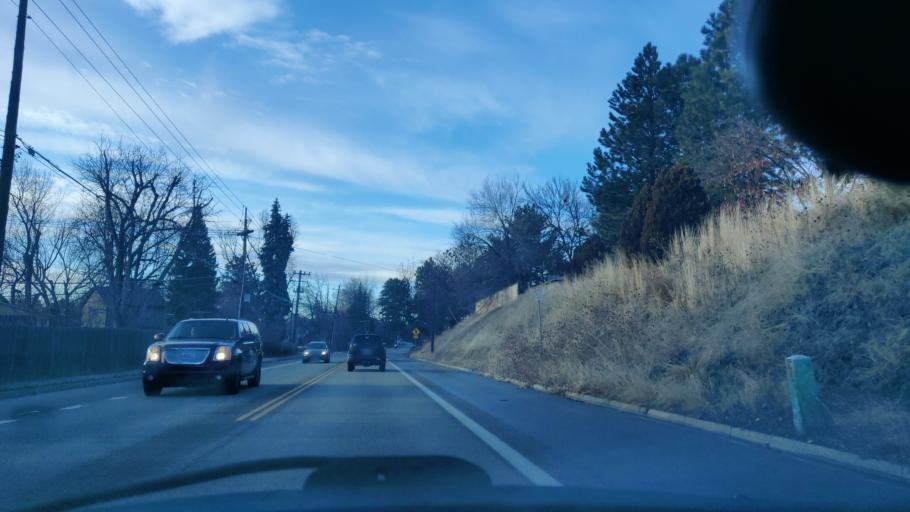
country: US
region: Idaho
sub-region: Ada County
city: Boise
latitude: 43.6421
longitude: -116.2120
